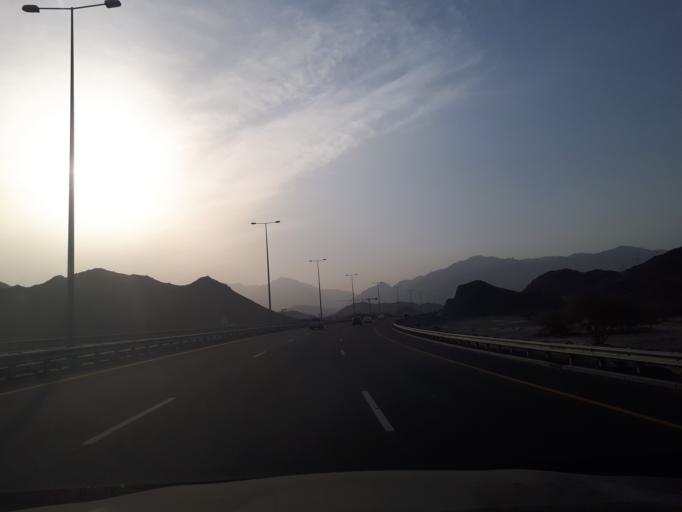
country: OM
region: Muhafazat ad Dakhiliyah
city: Bidbid
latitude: 23.3453
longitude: 58.0969
